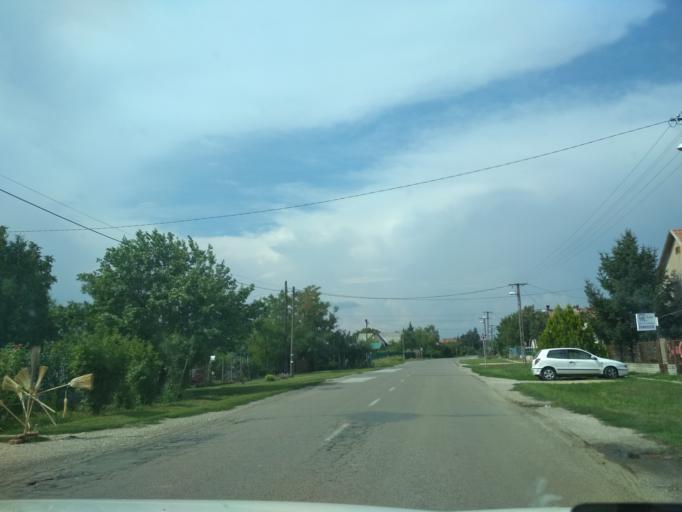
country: HU
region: Jasz-Nagykun-Szolnok
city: Tiszaszolos
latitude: 47.5484
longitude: 20.7214
